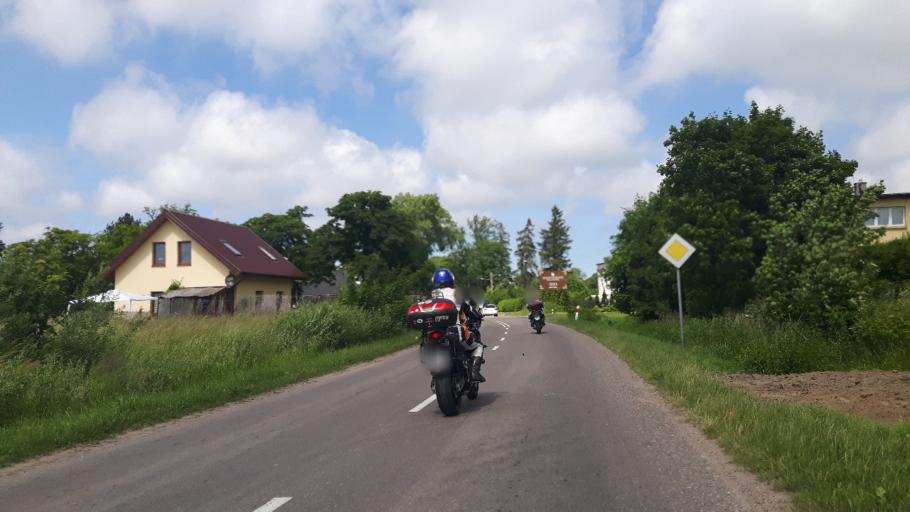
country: PL
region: Pomeranian Voivodeship
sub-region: Powiat slupski
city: Ustka
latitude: 54.5364
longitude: 16.8215
